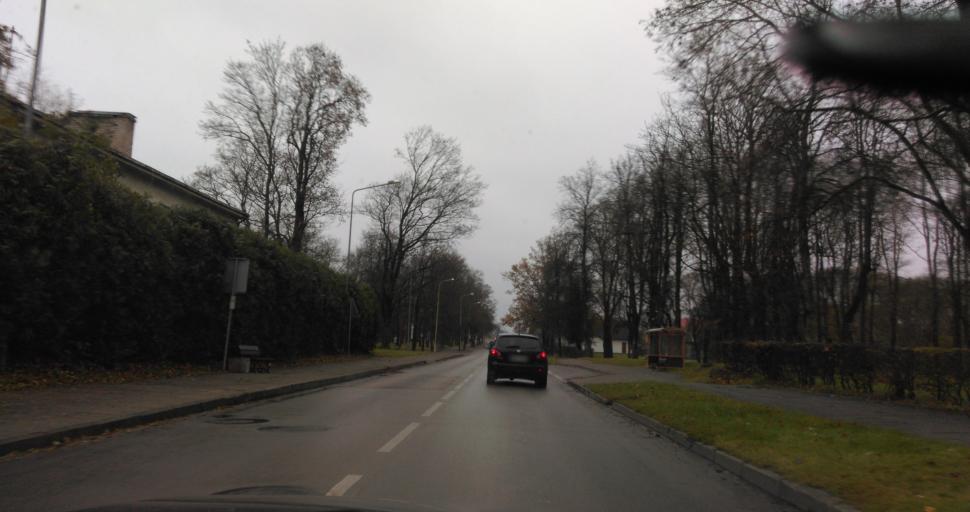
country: LT
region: Panevezys
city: Rokiskis
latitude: 55.9682
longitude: 25.5854
